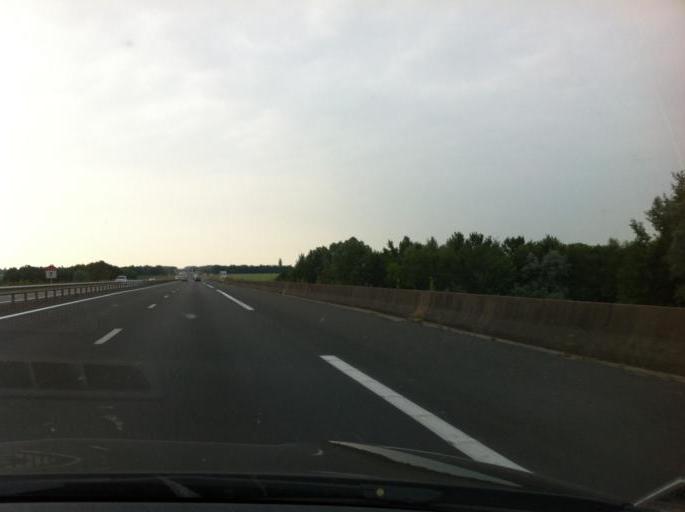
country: FR
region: Ile-de-France
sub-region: Departement de Seine-et-Marne
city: Vert-Saint-Denis
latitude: 48.5928
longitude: 2.6358
